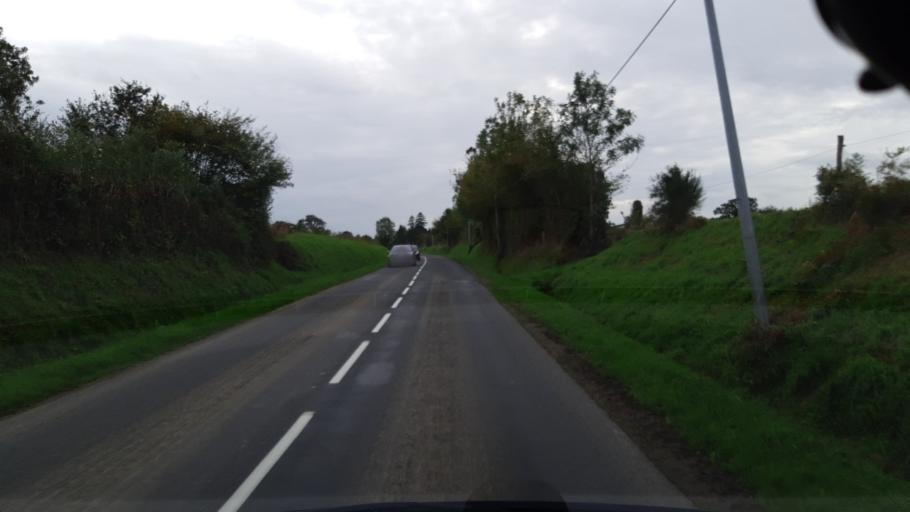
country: FR
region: Lower Normandy
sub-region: Departement de la Manche
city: Percy
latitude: 48.9987
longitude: -1.1955
